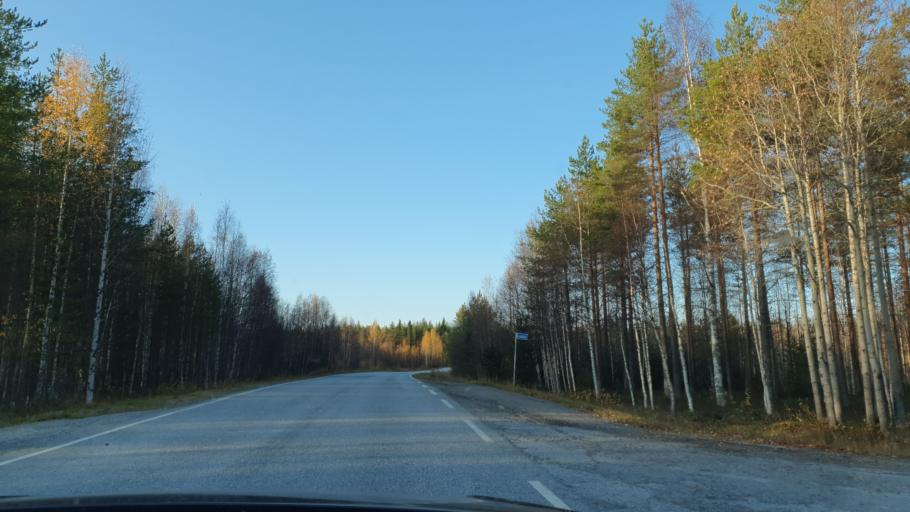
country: FI
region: Kainuu
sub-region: Kehys-Kainuu
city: Kuhmo
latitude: 64.3896
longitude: 29.4693
